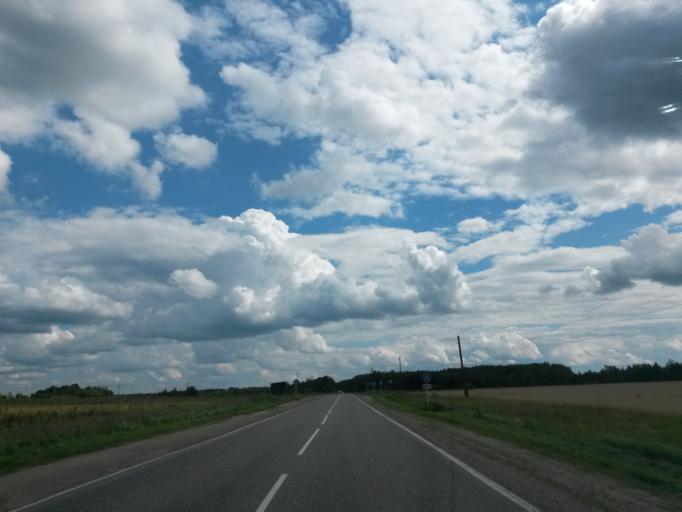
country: RU
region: Ivanovo
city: Pistsovo
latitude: 57.1293
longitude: 40.5997
